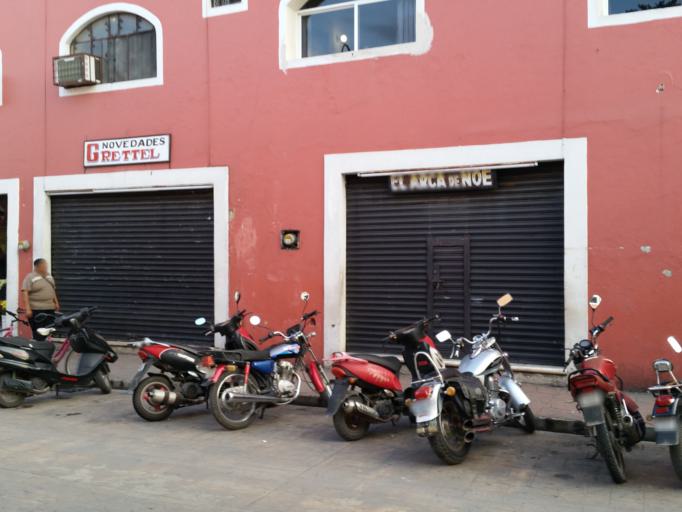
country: MX
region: Yucatan
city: Valladolid
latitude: 20.6907
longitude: -88.2025
